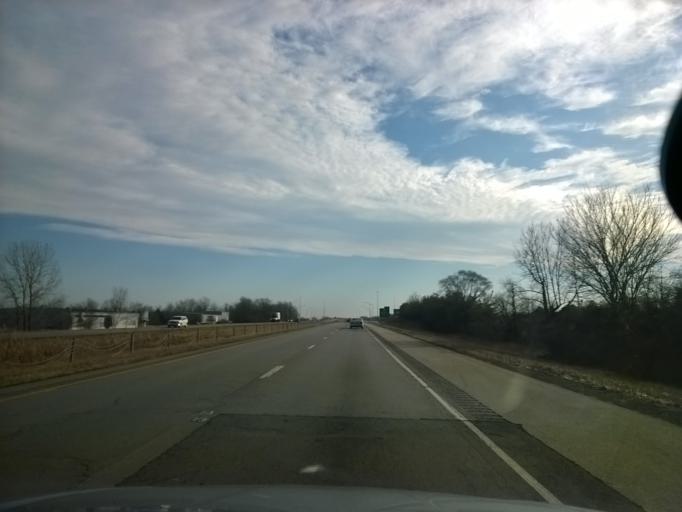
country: US
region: Indiana
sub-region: Johnson County
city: Franklin
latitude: 39.4920
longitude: -86.0166
